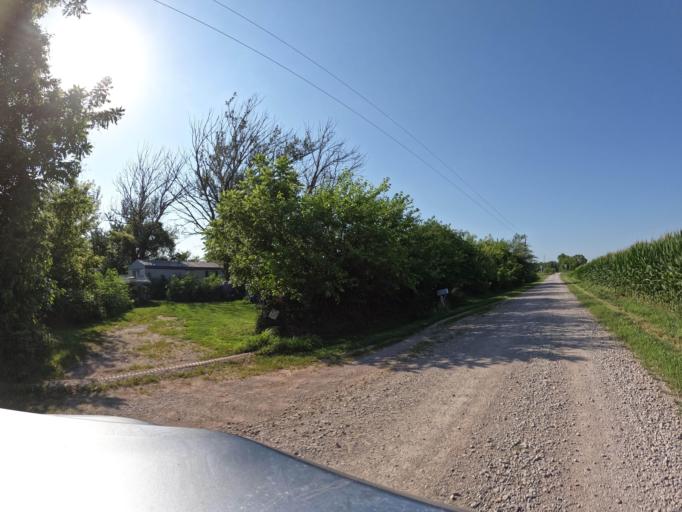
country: US
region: Iowa
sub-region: Appanoose County
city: Centerville
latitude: 40.7250
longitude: -93.0158
